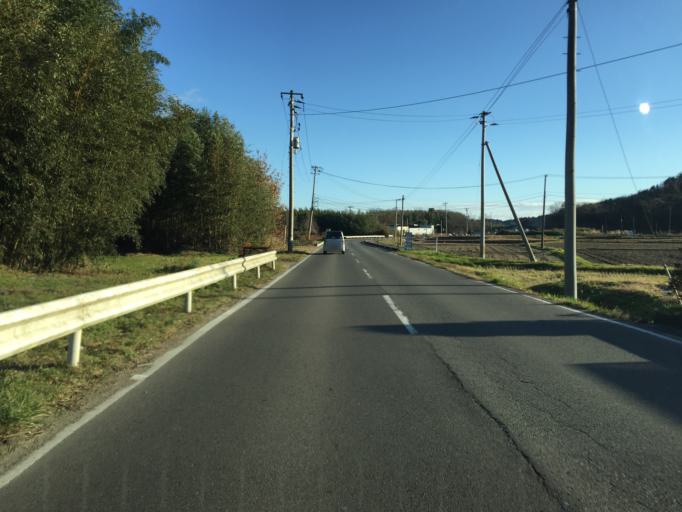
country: JP
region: Fukushima
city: Iwaki
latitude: 37.1146
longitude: 140.8609
